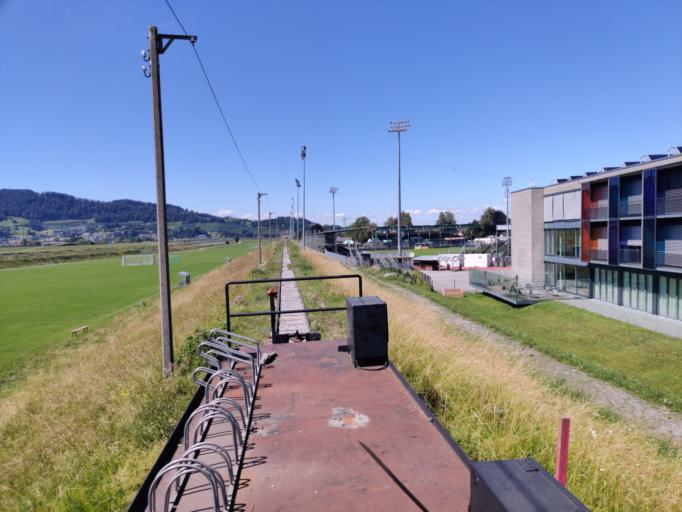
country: AT
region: Vorarlberg
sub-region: Politischer Bezirk Dornbirn
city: Lustenau
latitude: 47.4194
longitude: 9.6525
